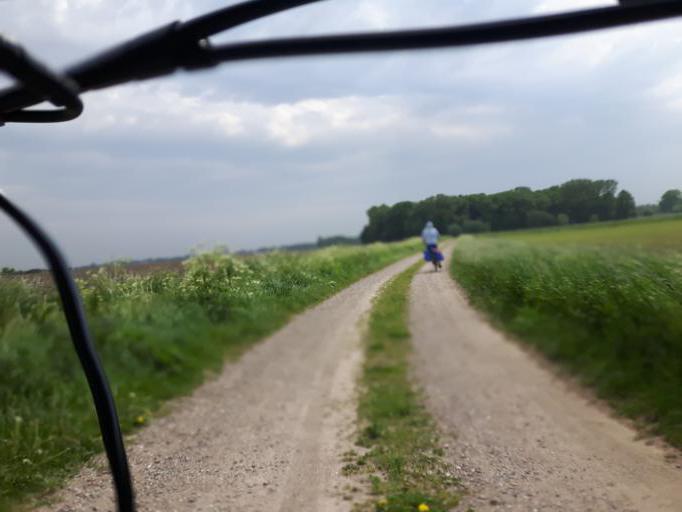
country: NL
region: North Brabant
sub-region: Gemeente Steenbergen
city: Kruisland
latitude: 51.5462
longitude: 4.3805
